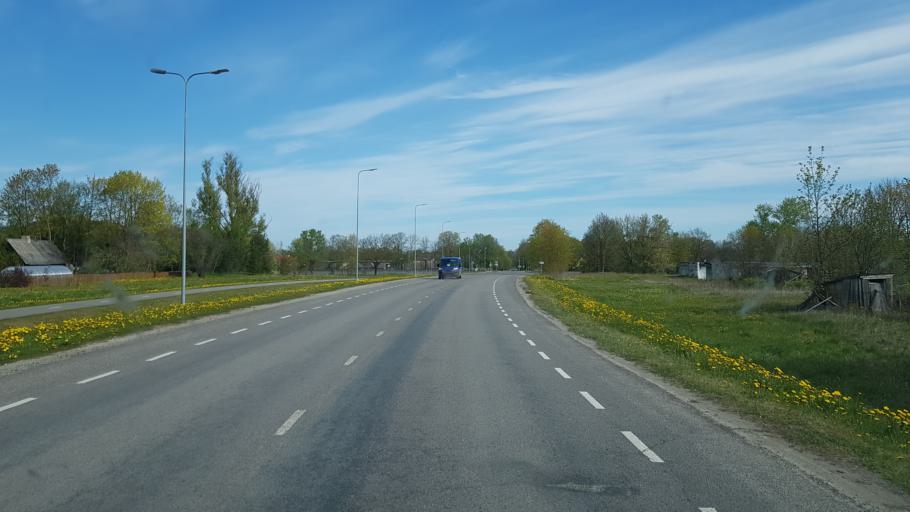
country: EE
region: Ida-Virumaa
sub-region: Kivioli linn
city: Kivioli
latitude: 59.3507
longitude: 26.9671
